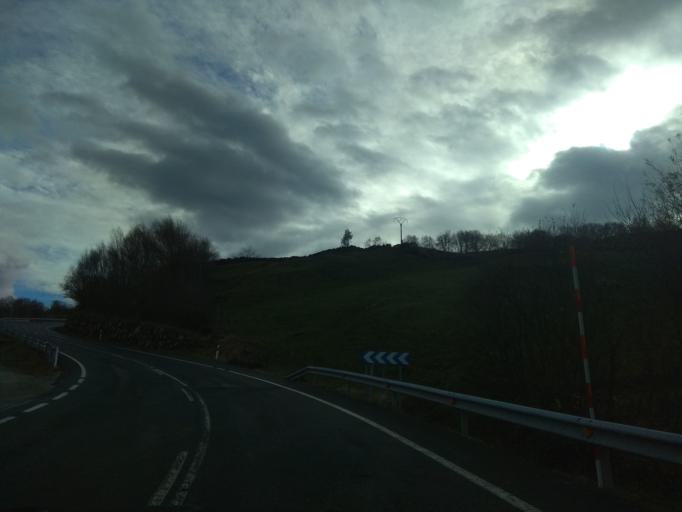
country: ES
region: Cantabria
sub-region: Provincia de Cantabria
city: San Pedro del Romeral
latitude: 43.0737
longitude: -3.8891
